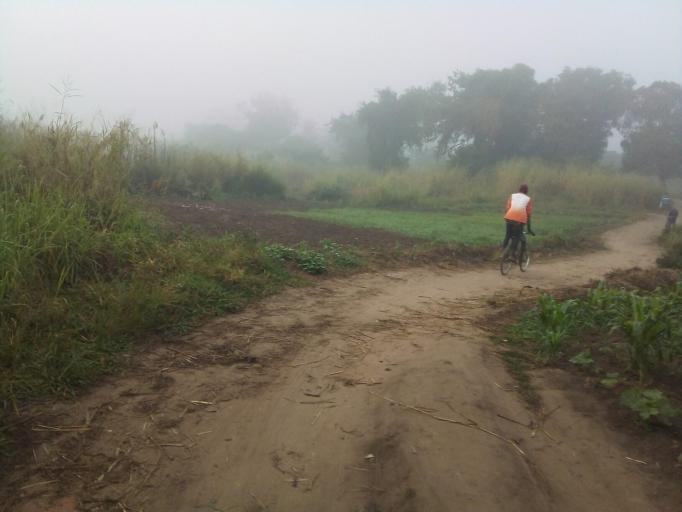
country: MZ
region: Zambezia
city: Quelimane
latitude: -17.5931
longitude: 36.6875
